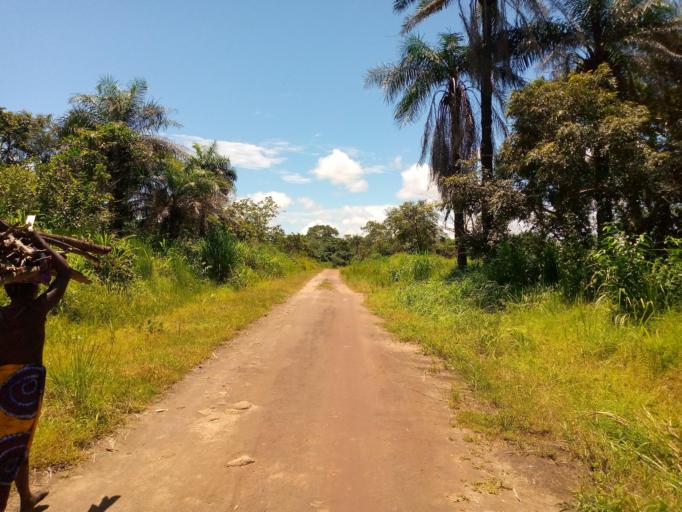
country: SL
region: Northern Province
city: Binkolo
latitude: 9.1047
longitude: -12.1403
